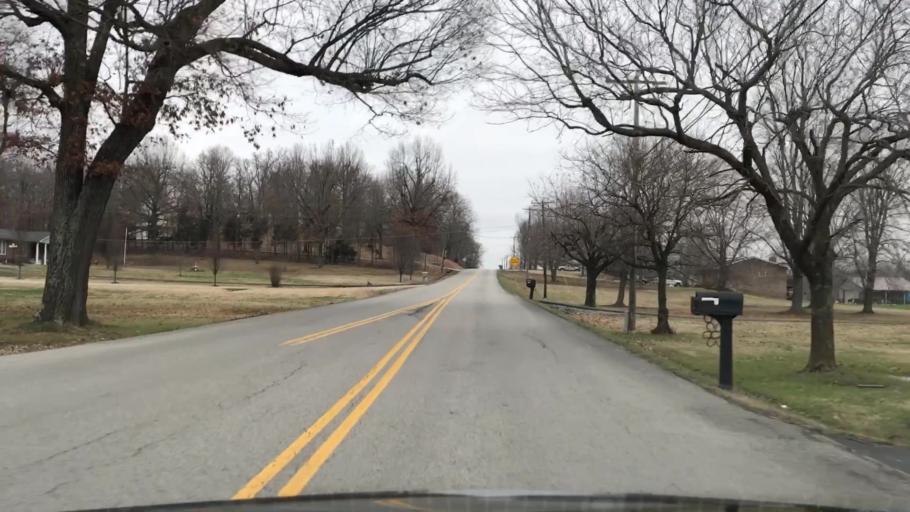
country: US
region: Kentucky
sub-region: Muhlenberg County
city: Greenville
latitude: 37.2245
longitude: -87.1936
